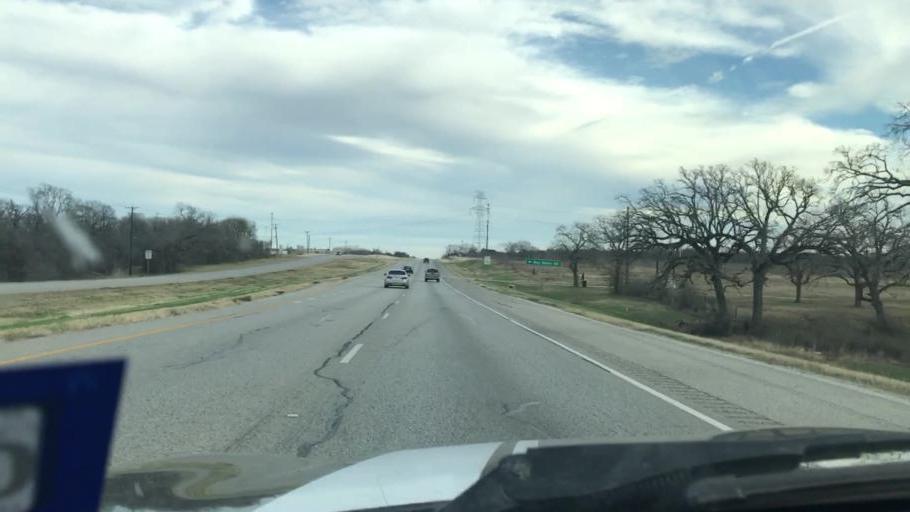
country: US
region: Texas
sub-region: Bastrop County
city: Elgin
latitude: 30.3319
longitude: -97.3515
